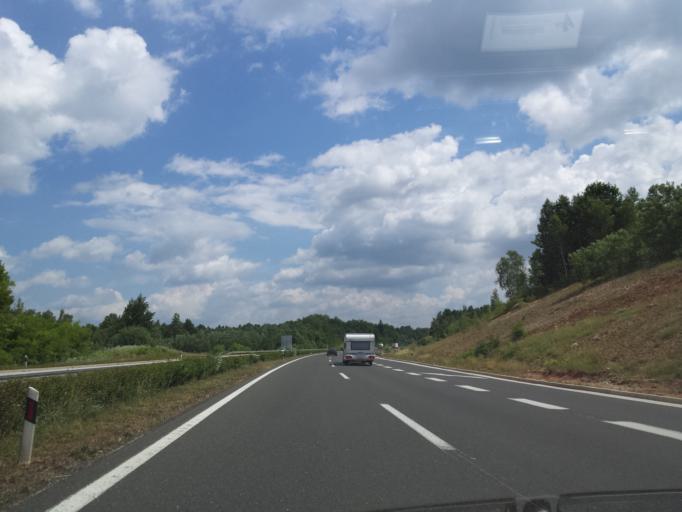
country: HR
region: Karlovacka
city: Ozalj
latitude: 45.4587
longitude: 15.3791
